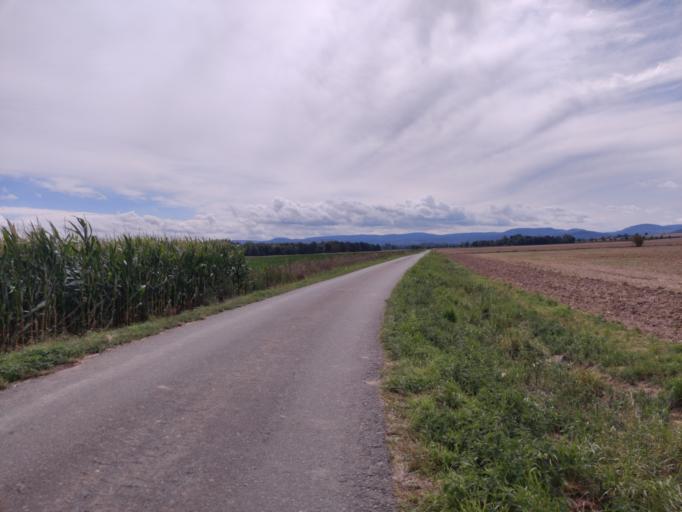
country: DE
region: Lower Saxony
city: Liebenburg
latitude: 51.9982
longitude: 10.3712
